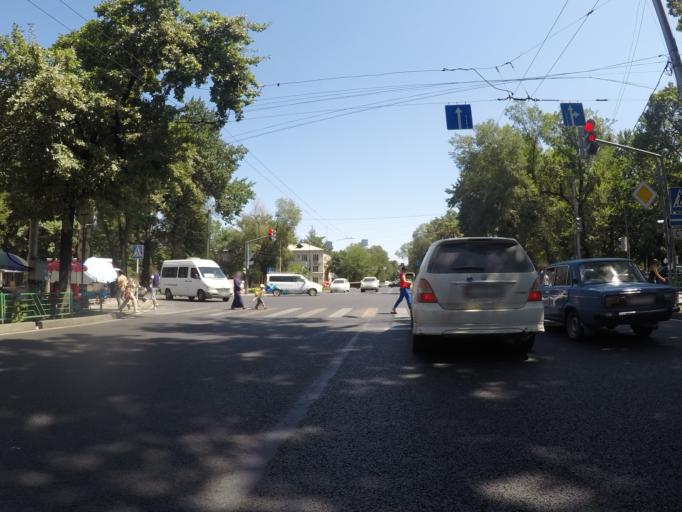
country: KG
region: Chuy
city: Bishkek
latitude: 42.8772
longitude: 74.5749
